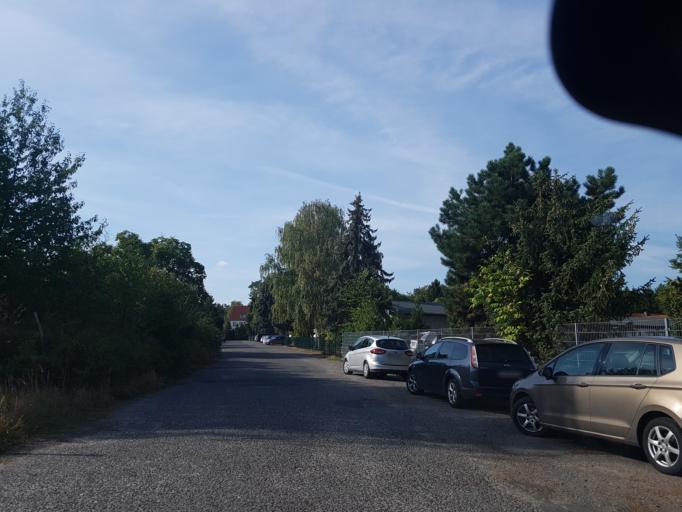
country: DE
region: Brandenburg
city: Belzig
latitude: 52.1482
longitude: 12.5748
